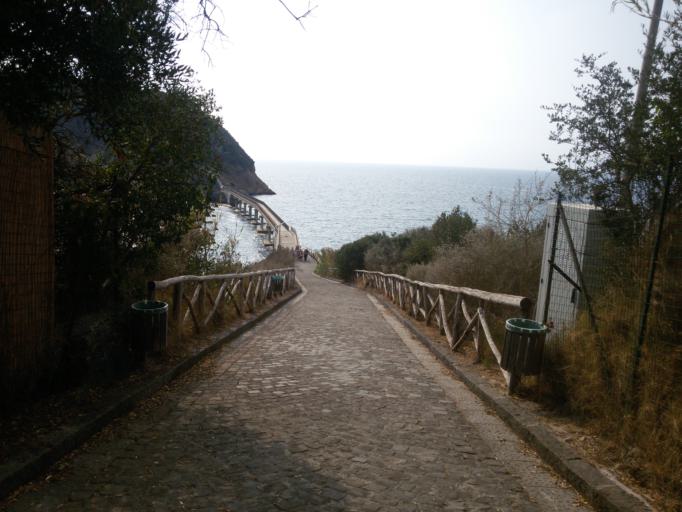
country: IT
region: Campania
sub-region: Provincia di Napoli
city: Procida
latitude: 40.7474
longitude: 14.0010
